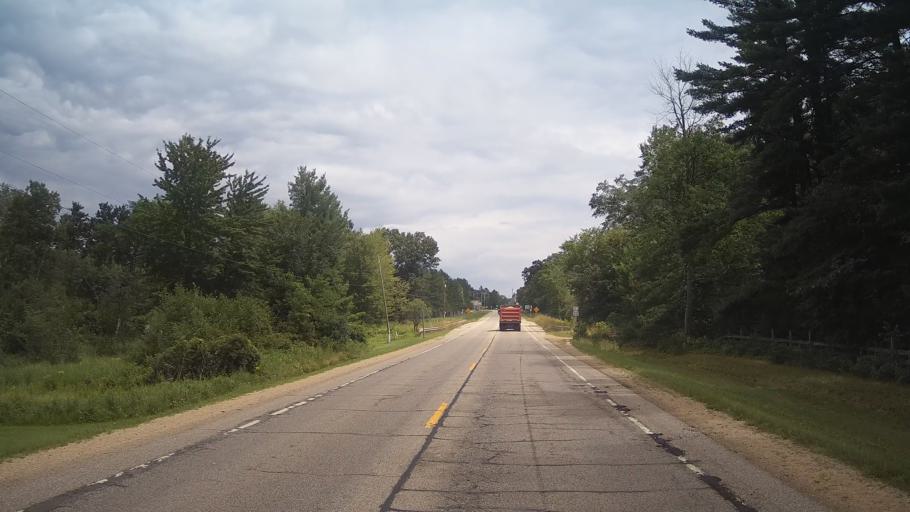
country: US
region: Wisconsin
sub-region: Waushara County
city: Wautoma
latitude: 44.0684
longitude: -89.3043
